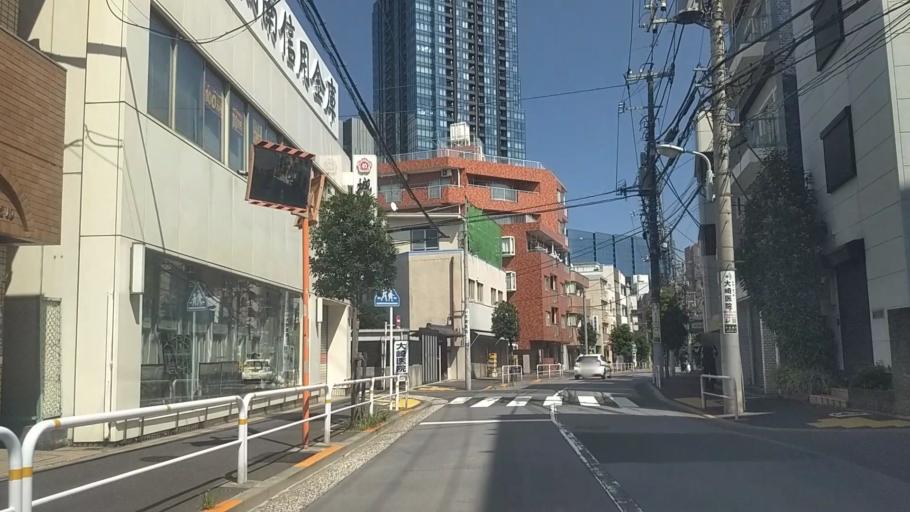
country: JP
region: Tokyo
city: Tokyo
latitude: 35.6170
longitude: 139.7244
